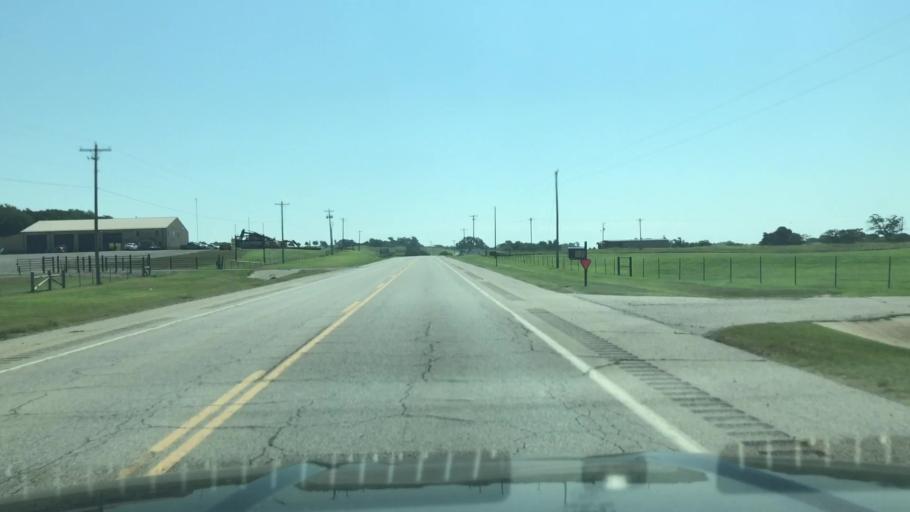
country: US
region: Oklahoma
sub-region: Creek County
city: Drumright
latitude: 35.9884
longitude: -96.5564
